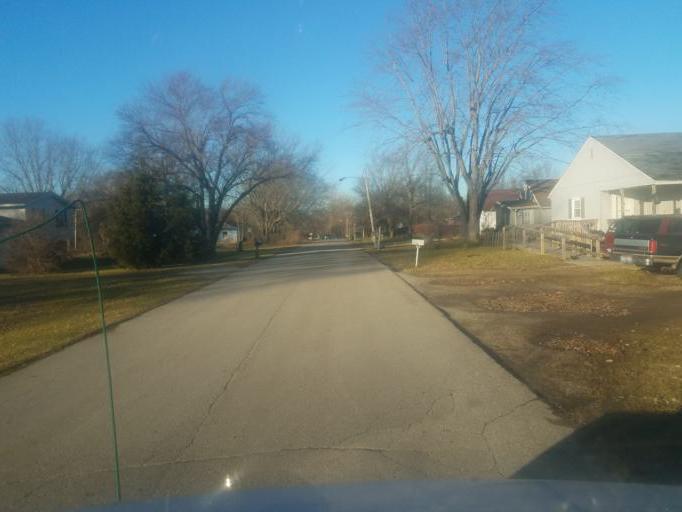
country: US
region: Ohio
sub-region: Richland County
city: Mansfield
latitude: 40.7893
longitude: -82.5401
